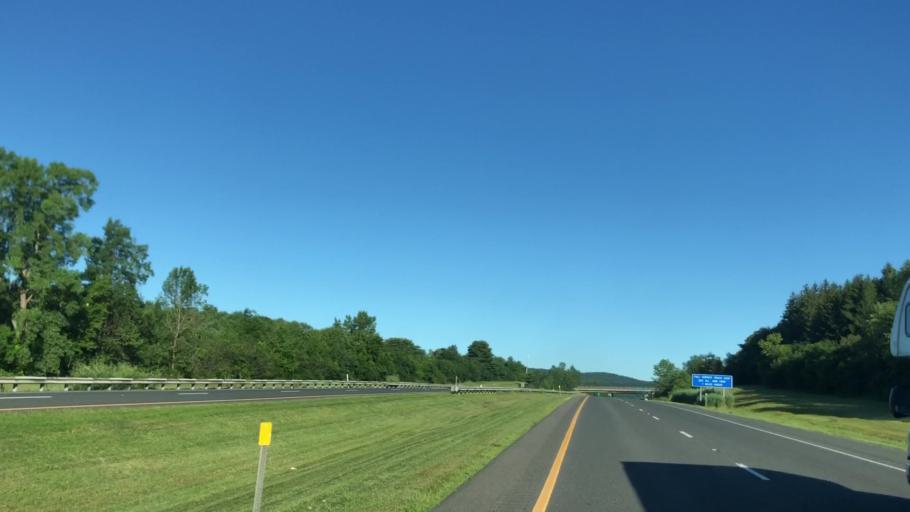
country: US
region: Massachusetts
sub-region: Berkshire County
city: Stockbridge
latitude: 42.3000
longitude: -73.3121
